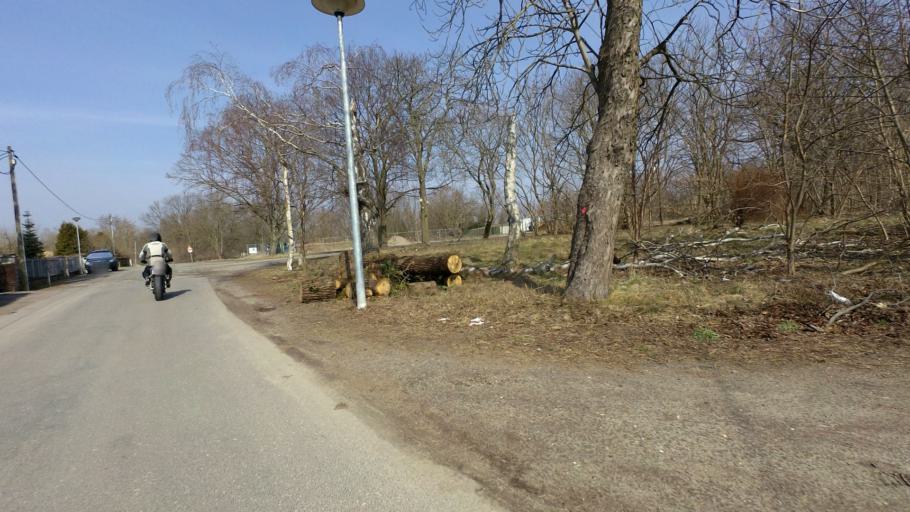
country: DE
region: Brandenburg
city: Werder
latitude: 52.3878
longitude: 12.9202
